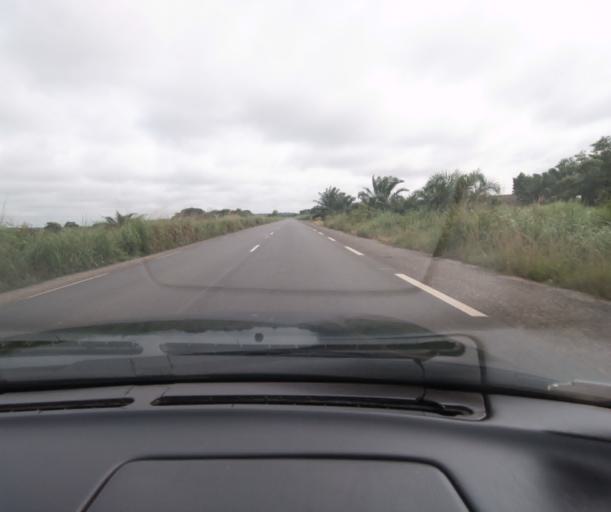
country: CM
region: Centre
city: Saa
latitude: 4.3821
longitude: 11.2561
